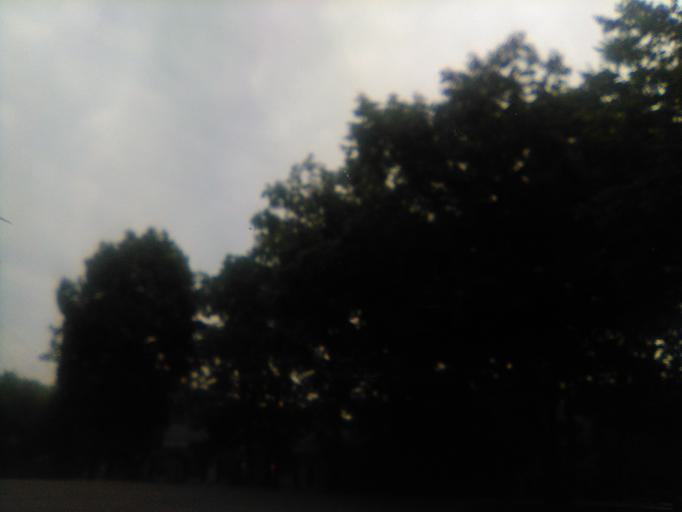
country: US
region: Tennessee
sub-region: Davidson County
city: Belle Meade
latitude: 36.1133
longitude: -86.8906
